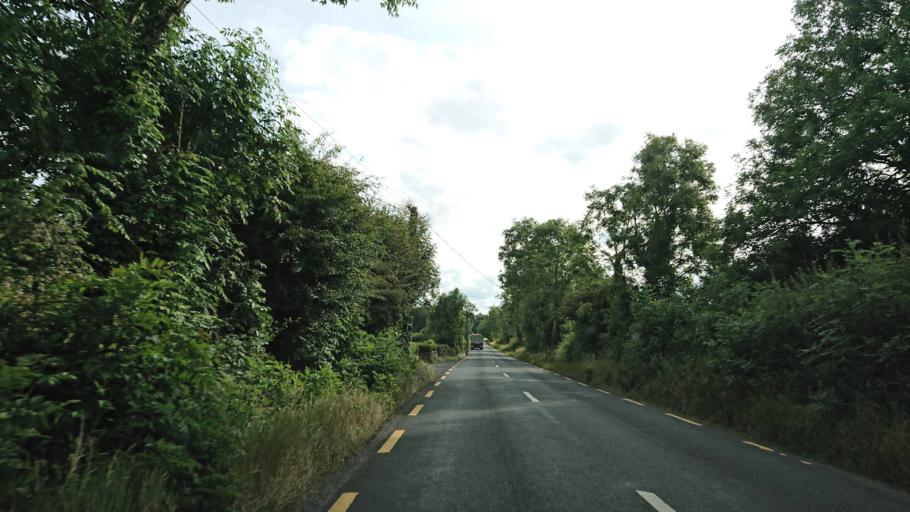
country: IE
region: Connaught
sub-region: County Leitrim
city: Carrick-on-Shannon
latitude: 53.9705
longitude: -8.0655
